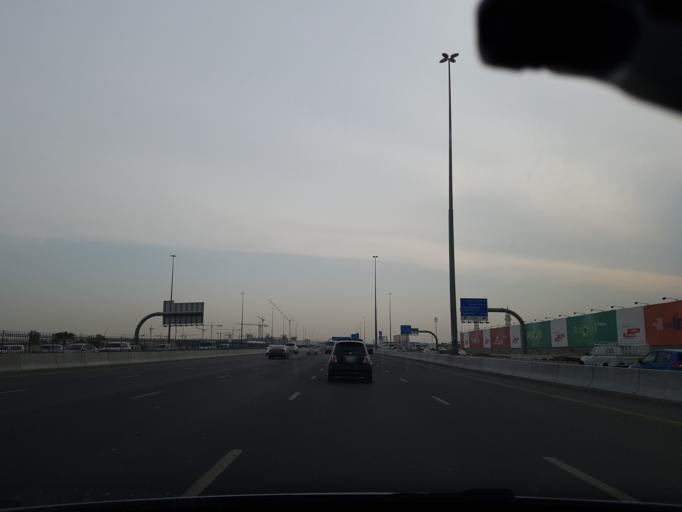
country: AE
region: Ash Shariqah
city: Sharjah
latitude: 25.3282
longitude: 55.4606
